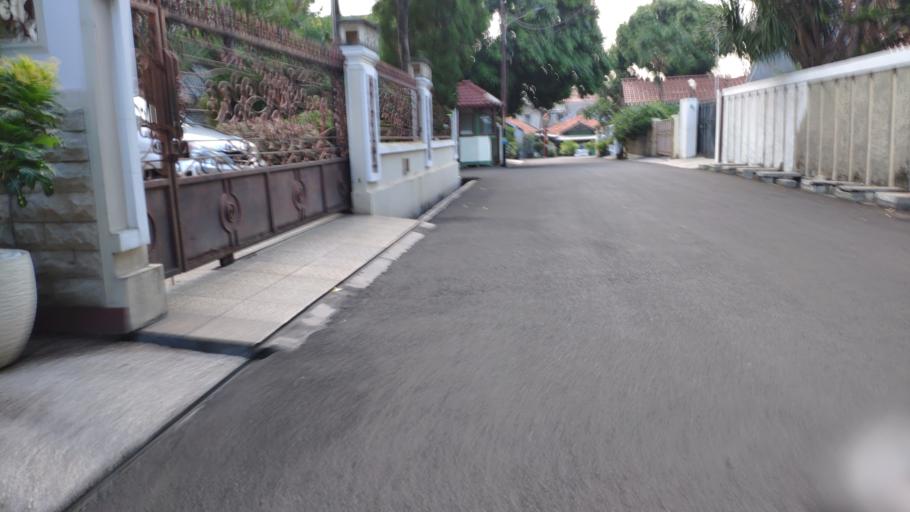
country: ID
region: Jakarta Raya
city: Jakarta
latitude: -6.2991
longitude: 106.8226
